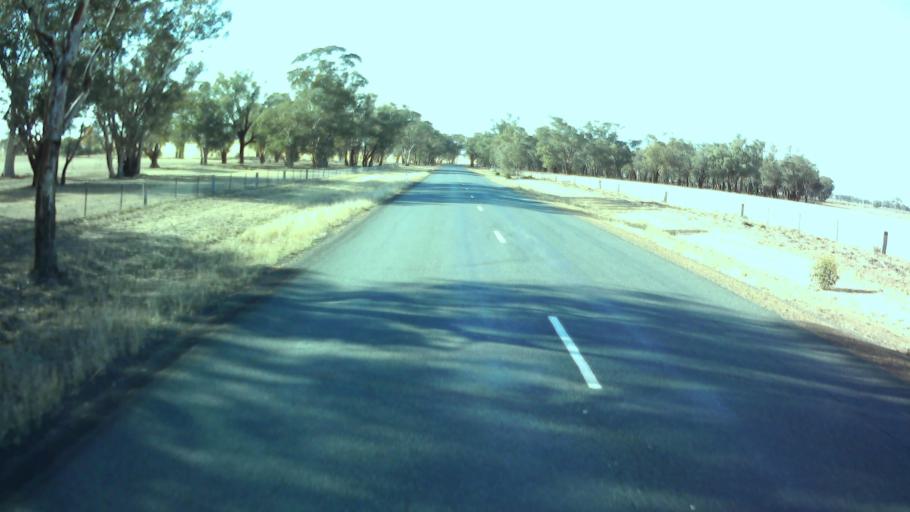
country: AU
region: New South Wales
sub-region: Weddin
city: Grenfell
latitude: -33.9474
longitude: 148.1367
